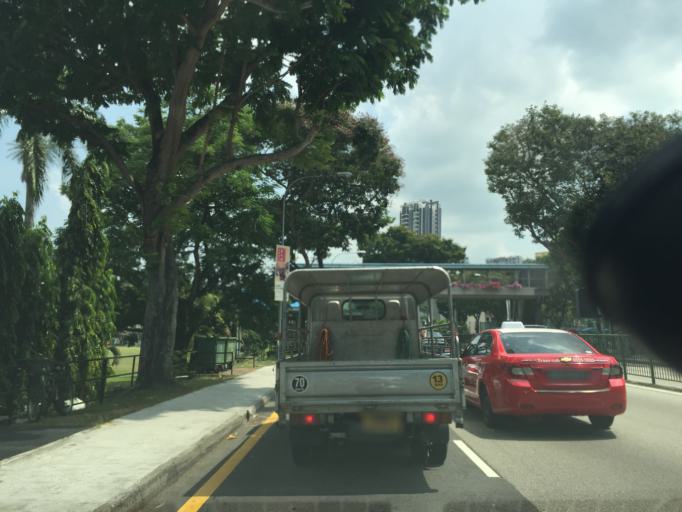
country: SG
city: Singapore
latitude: 1.3181
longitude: 103.8555
